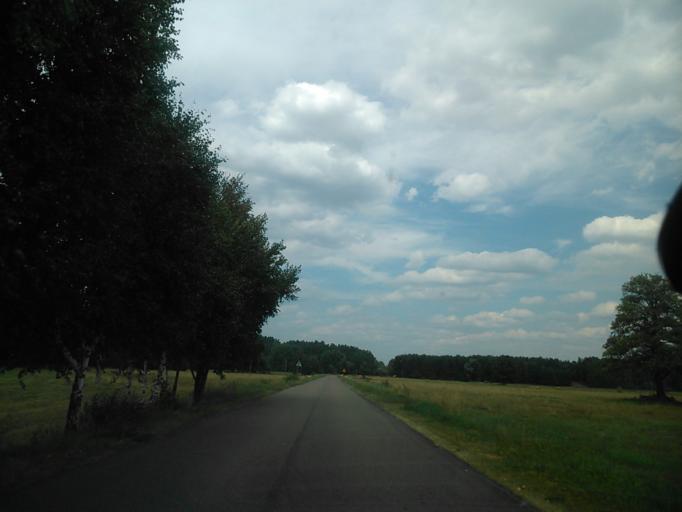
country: PL
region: Masovian Voivodeship
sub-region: Powiat ostrolecki
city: Czarnia
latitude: 53.3722
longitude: 21.1999
